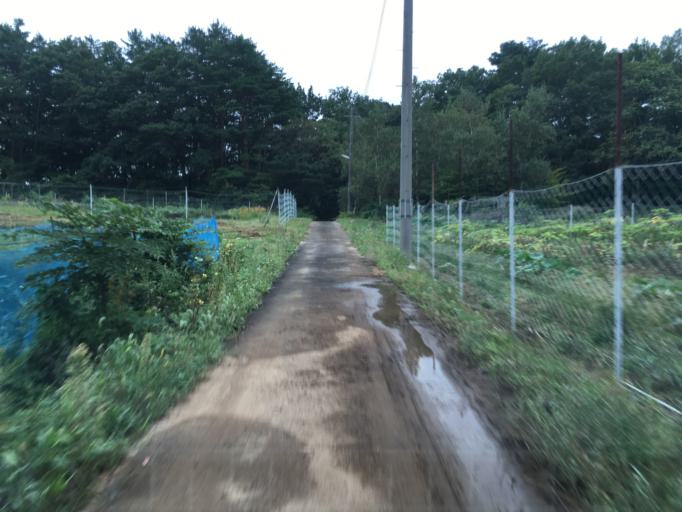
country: JP
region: Fukushima
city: Fukushima-shi
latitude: 37.8088
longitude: 140.3386
